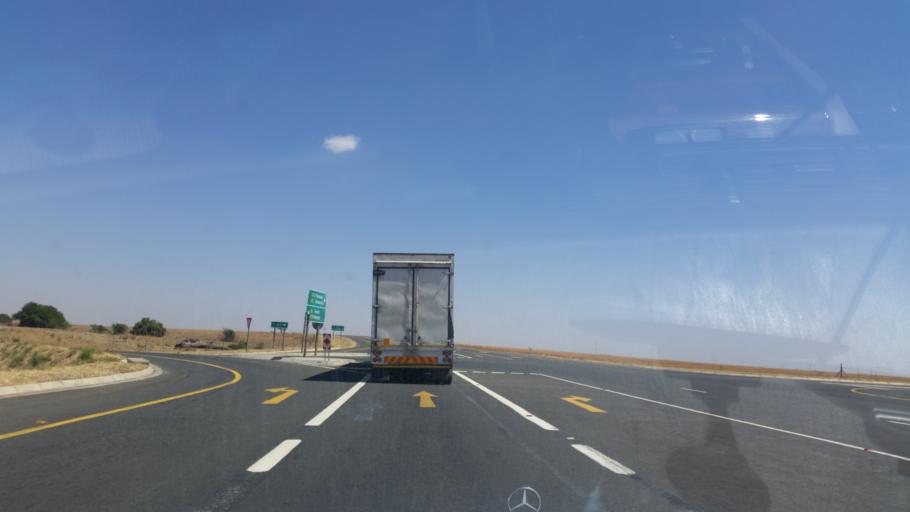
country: ZA
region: Orange Free State
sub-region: Lejweleputswa District Municipality
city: Winburg
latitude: -28.4941
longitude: 27.0352
